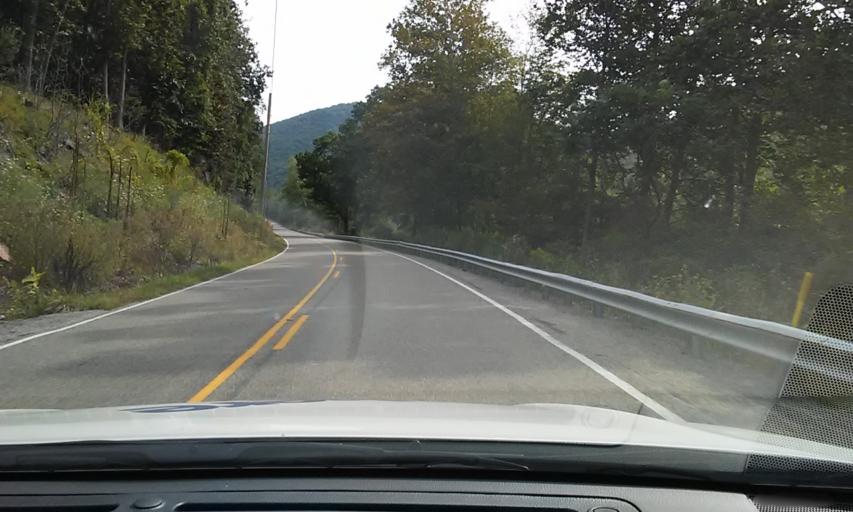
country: US
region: Pennsylvania
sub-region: Cameron County
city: Emporium
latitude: 41.3428
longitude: -78.2823
